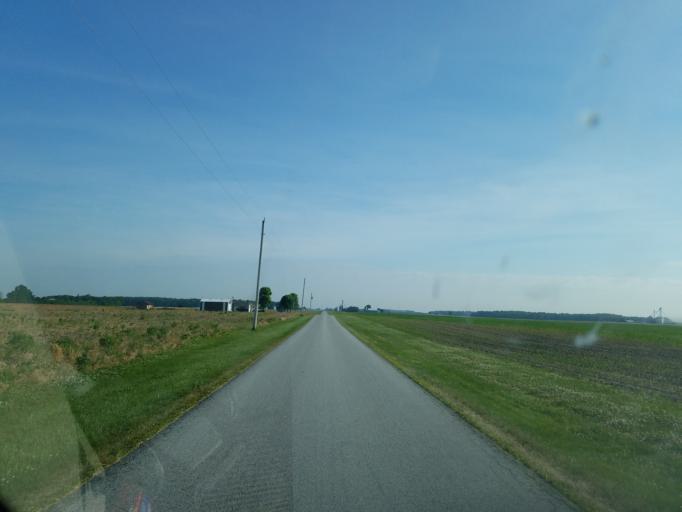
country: US
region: Ohio
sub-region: Hardin County
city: Kenton
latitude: 40.7371
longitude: -83.6717
